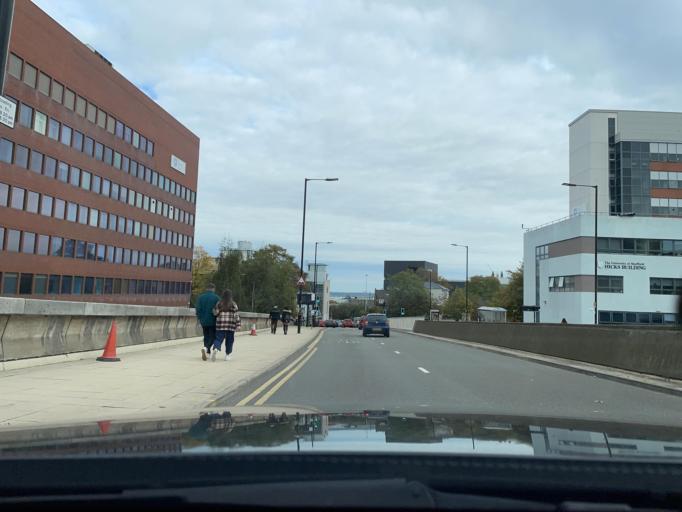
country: GB
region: England
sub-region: Sheffield
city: Sheffield
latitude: 53.3812
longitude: -1.4879
